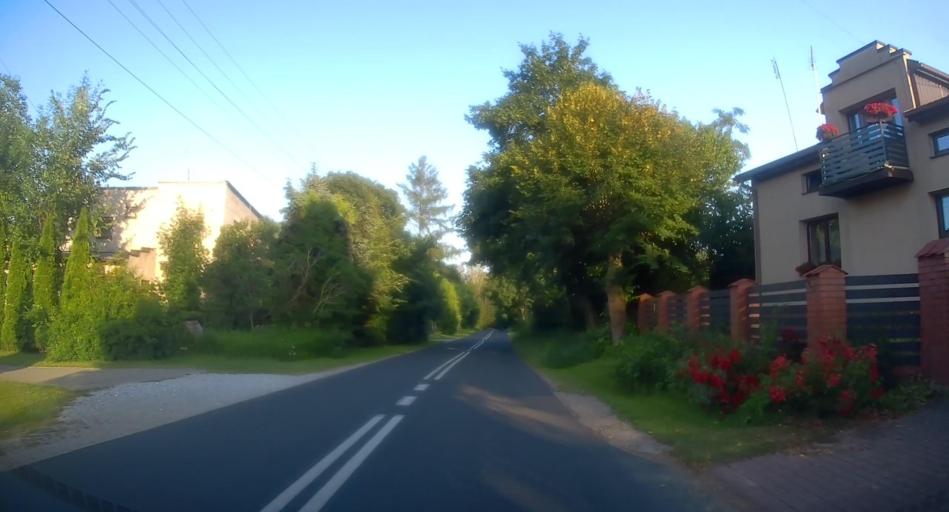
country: PL
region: Lodz Voivodeship
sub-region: Powiat skierniewicki
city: Kowiesy
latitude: 51.8979
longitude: 20.3750
